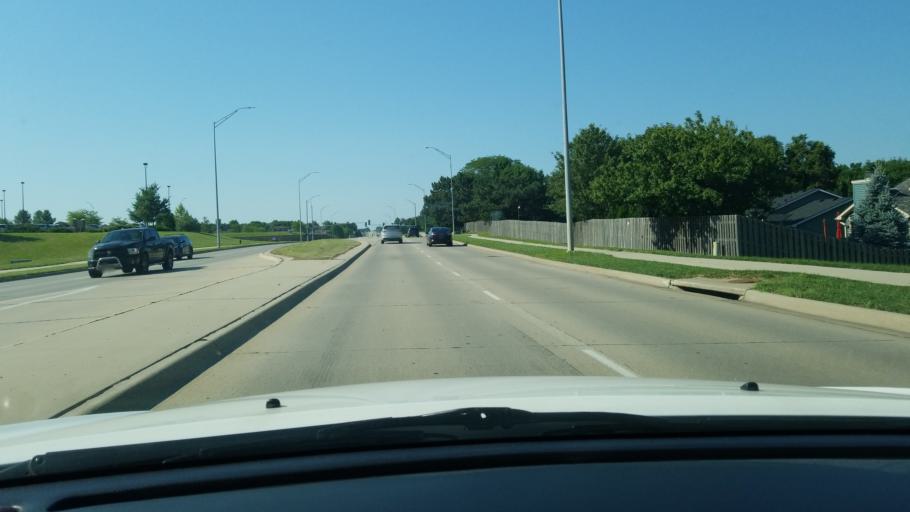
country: US
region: Nebraska
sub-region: Lancaster County
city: Lincoln
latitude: 40.7721
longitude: -96.6062
